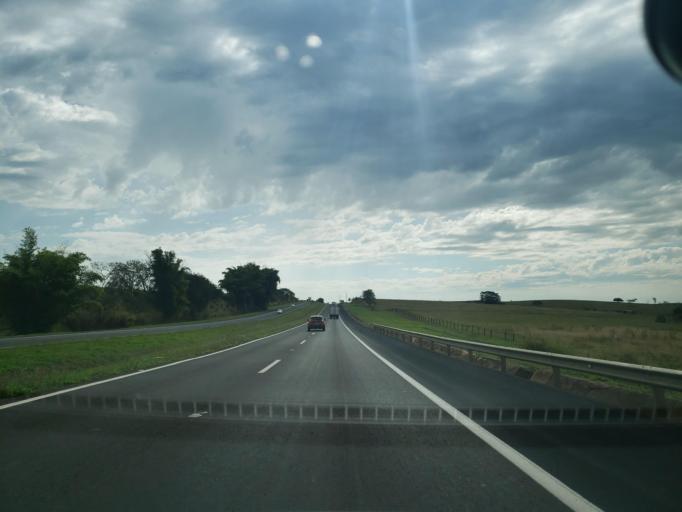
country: BR
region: Sao Paulo
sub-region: Cafelandia
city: Cafelandia
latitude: -21.7838
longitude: -49.6559
